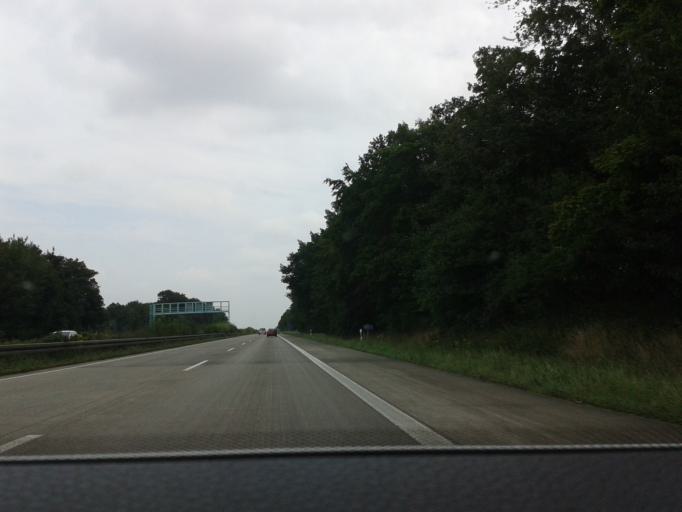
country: DE
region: North Rhine-Westphalia
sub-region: Regierungsbezirk Arnsberg
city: Welver
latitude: 51.5394
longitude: 8.0104
